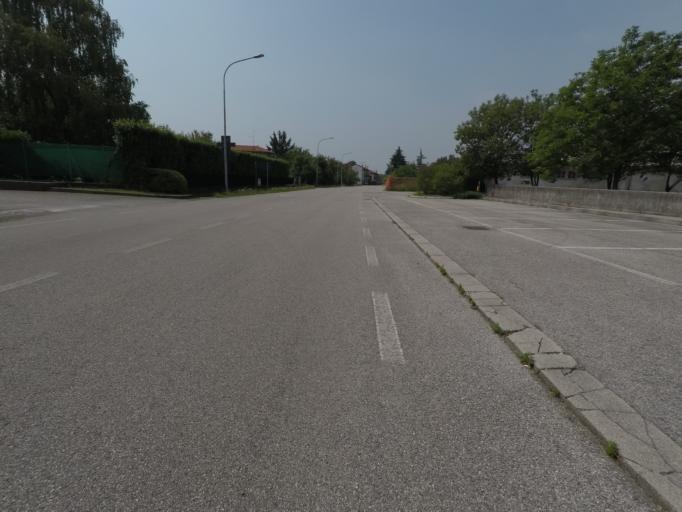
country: IT
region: Friuli Venezia Giulia
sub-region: Provincia di Pordenone
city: Montereale Valcellina
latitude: 46.1521
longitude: 12.6579
